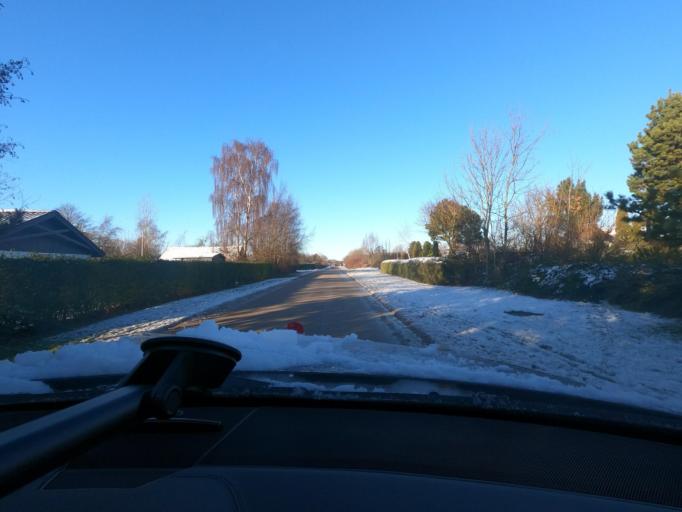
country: DK
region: South Denmark
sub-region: Sonderborg Kommune
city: Horuphav
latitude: 54.8760
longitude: 10.0168
